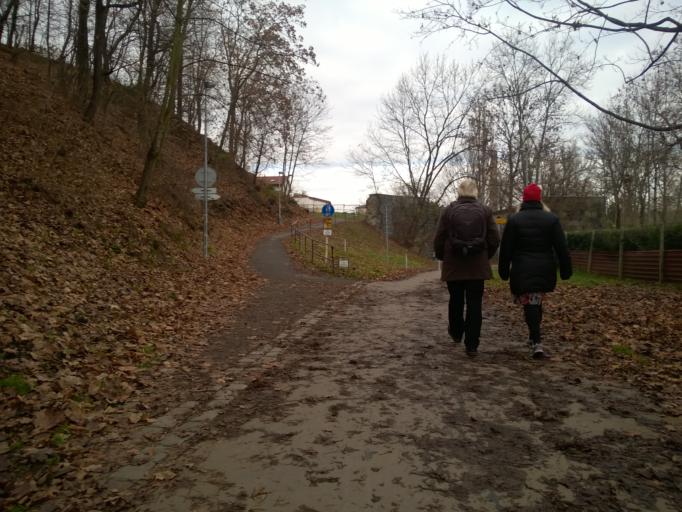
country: CZ
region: Praha
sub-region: Praha 1
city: Mala Strana
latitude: 50.1078
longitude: 14.4064
